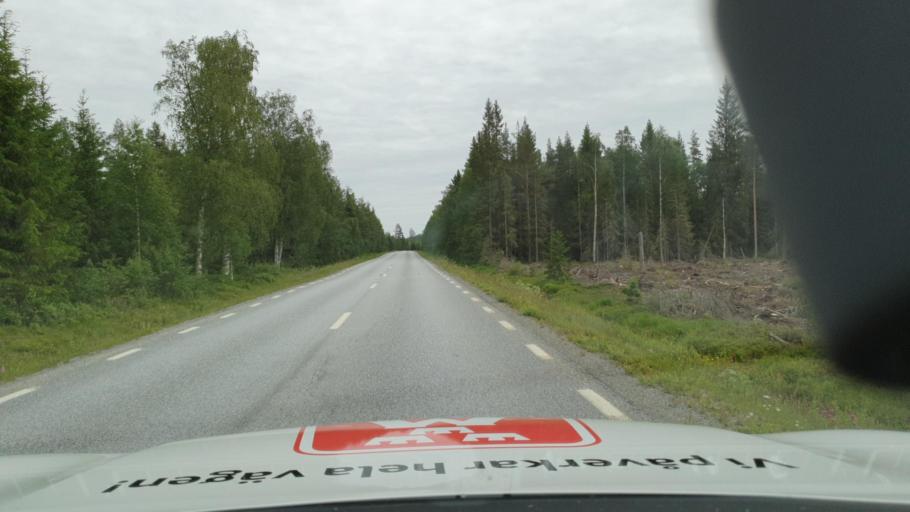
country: SE
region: Vaesterbotten
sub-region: Skelleftea Kommun
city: Burtraesk
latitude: 64.3986
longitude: 20.3270
